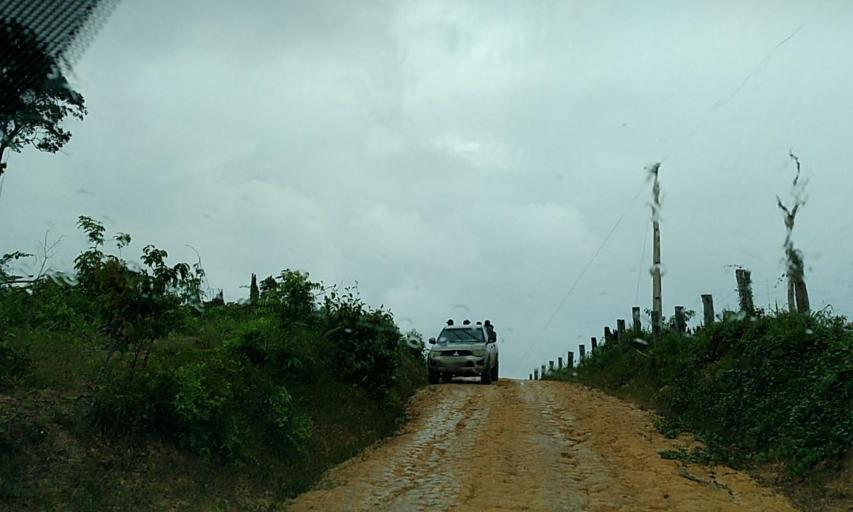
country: BR
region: Para
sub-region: Altamira
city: Altamira
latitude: -2.9503
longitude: -52.9008
